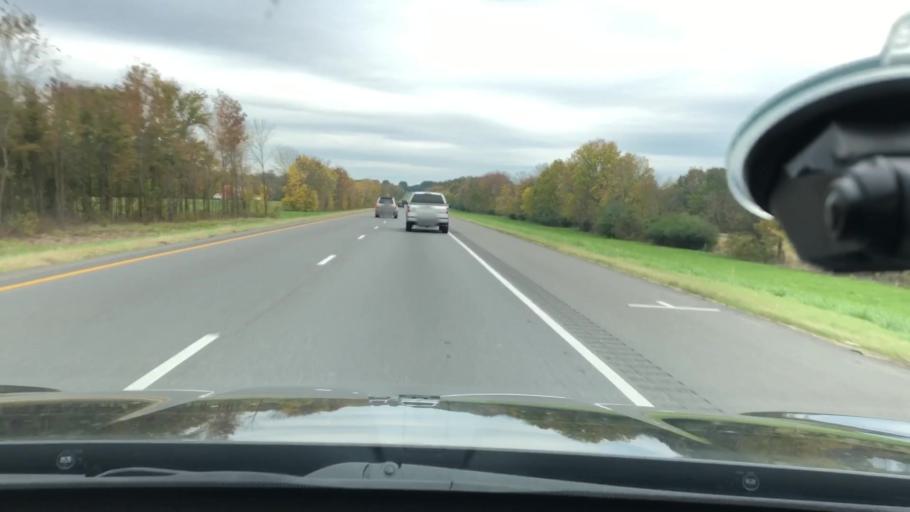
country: US
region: Arkansas
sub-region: Hempstead County
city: Hope
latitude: 33.7215
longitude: -93.5536
